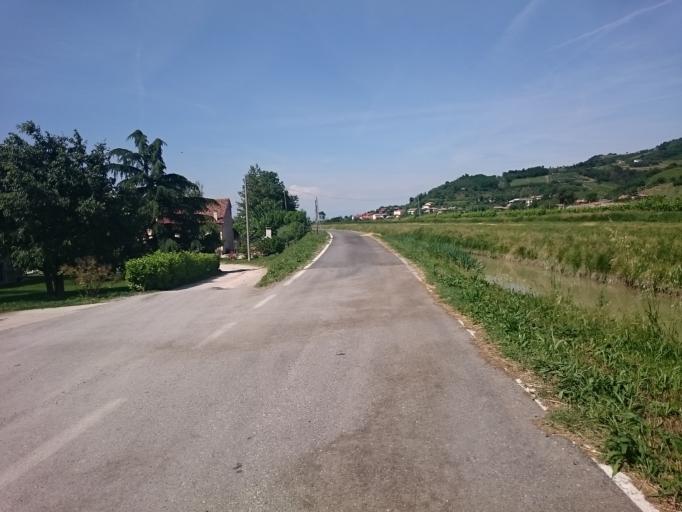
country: IT
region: Veneto
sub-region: Provincia di Padova
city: Vo
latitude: 45.3491
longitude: 11.6306
